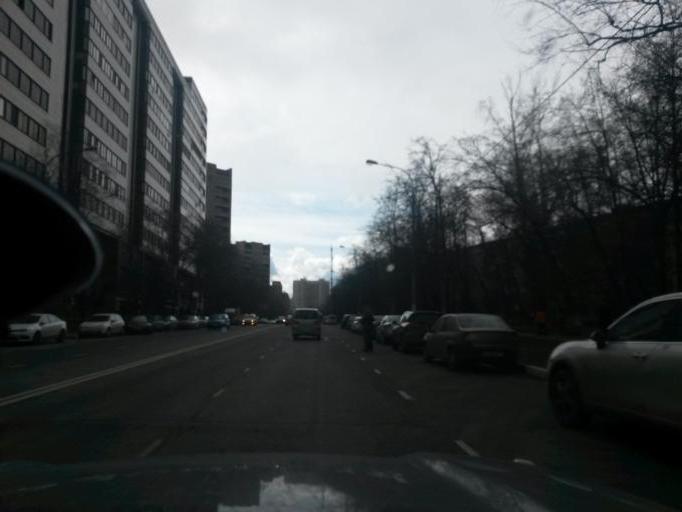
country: RU
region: Moskovskaya
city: Semenovskoye
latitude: 55.6802
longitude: 37.5465
